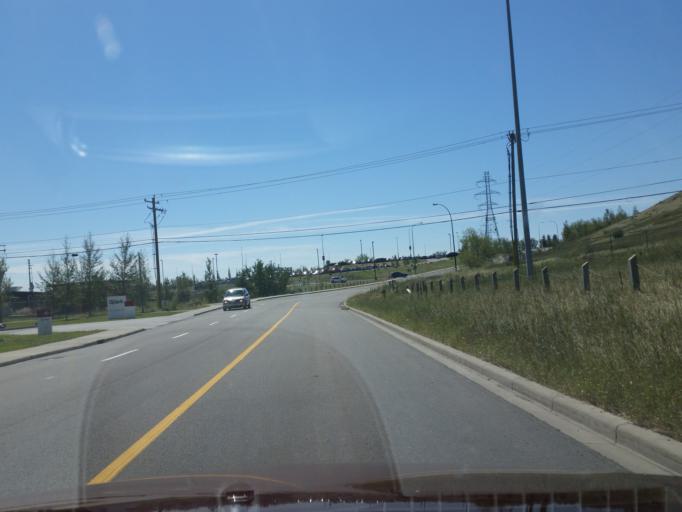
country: CA
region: Alberta
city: Calgary
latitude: 51.0529
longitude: -114.0263
